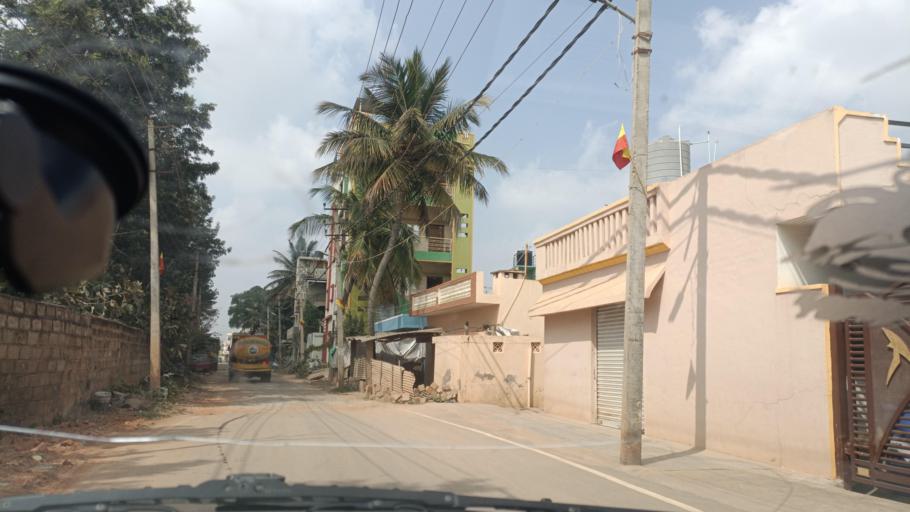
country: IN
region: Karnataka
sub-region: Bangalore Urban
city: Yelahanka
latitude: 13.1544
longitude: 77.6265
